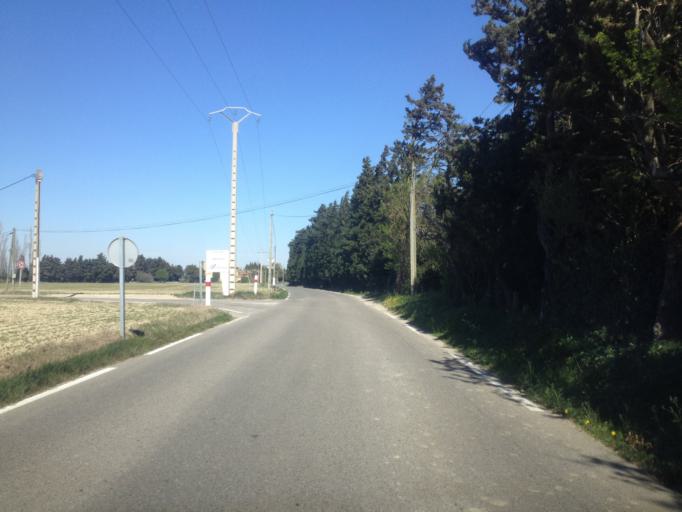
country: FR
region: Provence-Alpes-Cote d'Azur
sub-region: Departement du Vaucluse
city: Serignan-du-Comtat
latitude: 44.1652
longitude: 4.8348
